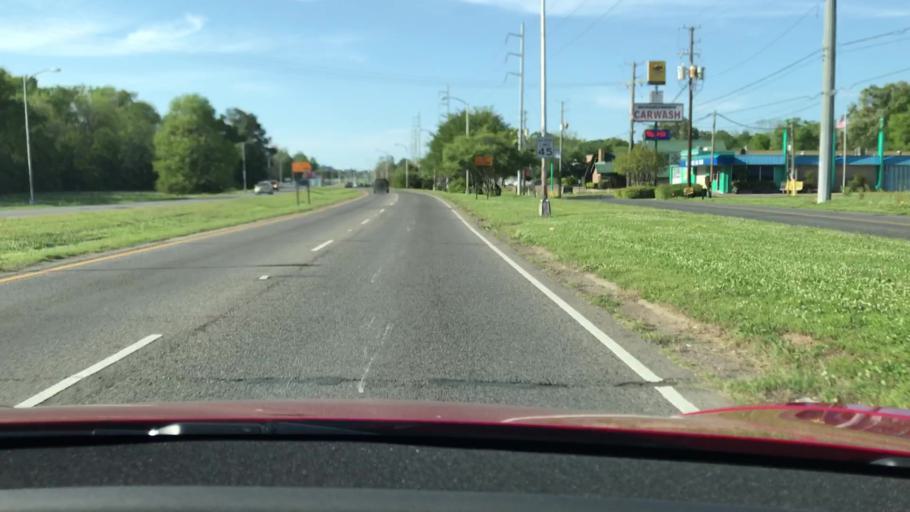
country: US
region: Louisiana
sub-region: Bossier Parish
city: Bossier City
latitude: 32.4857
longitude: -93.7240
